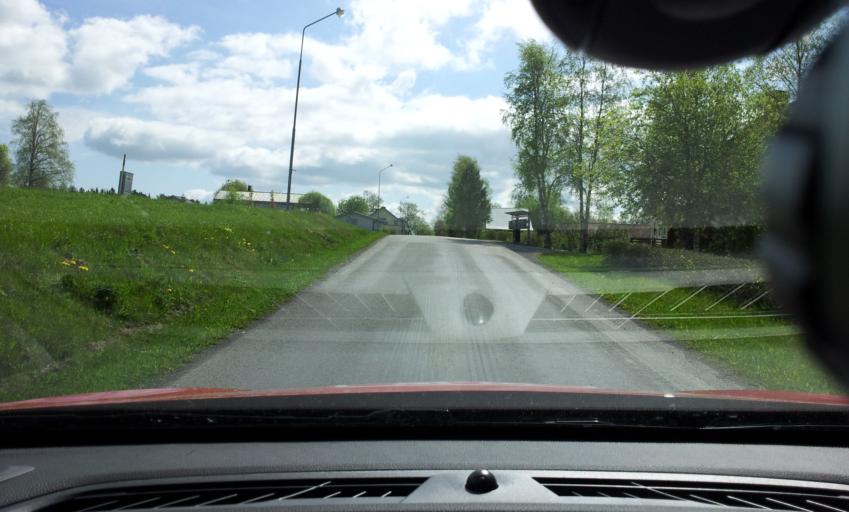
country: SE
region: Jaemtland
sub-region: OEstersunds Kommun
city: Ostersund
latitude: 63.0121
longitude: 14.6041
